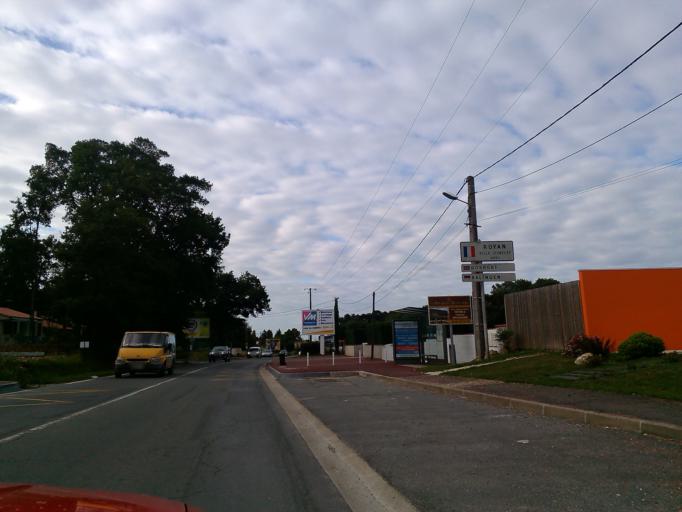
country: FR
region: Poitou-Charentes
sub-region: Departement de la Charente-Maritime
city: Royan
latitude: 45.6490
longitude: -1.0245
